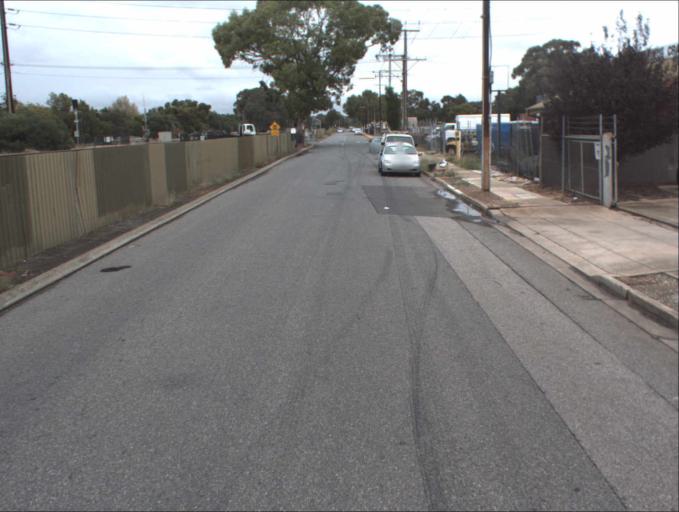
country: AU
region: South Australia
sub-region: Prospect
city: Prospect
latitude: -34.8810
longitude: 138.5828
